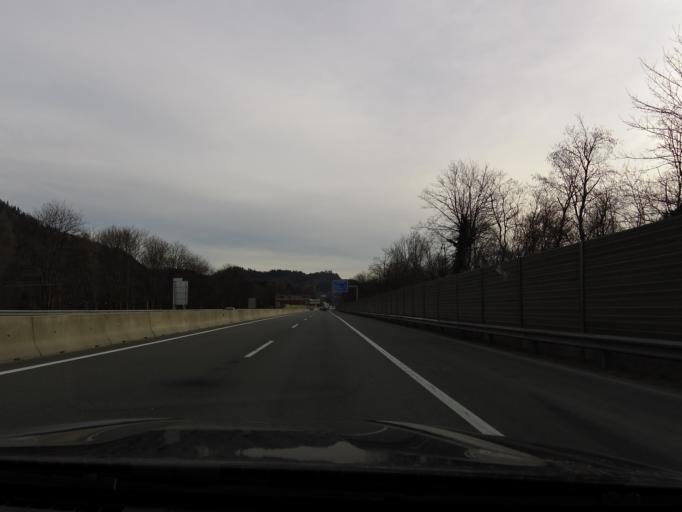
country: AT
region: Tyrol
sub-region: Politischer Bezirk Kufstein
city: Kufstein
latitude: 47.5771
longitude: 12.1475
